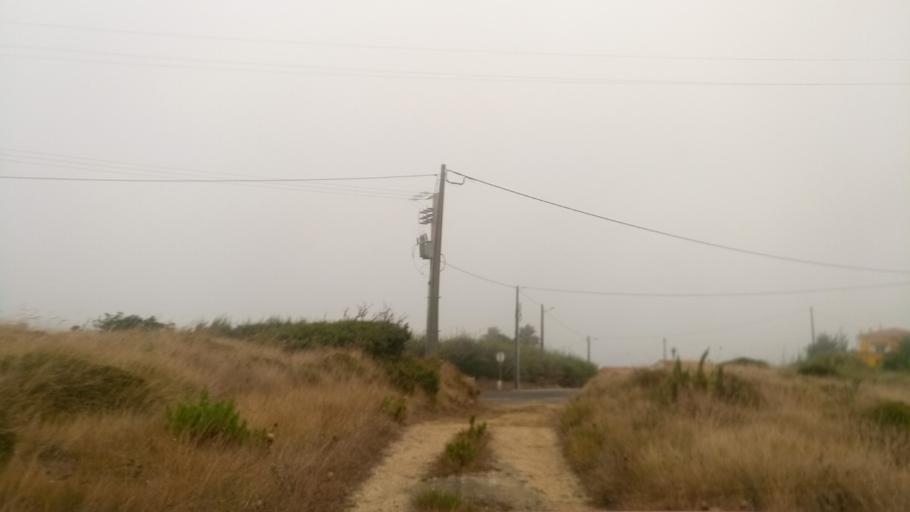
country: PT
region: Leiria
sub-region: Caldas da Rainha
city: Caldas da Rainha
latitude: 39.4651
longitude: -9.1959
